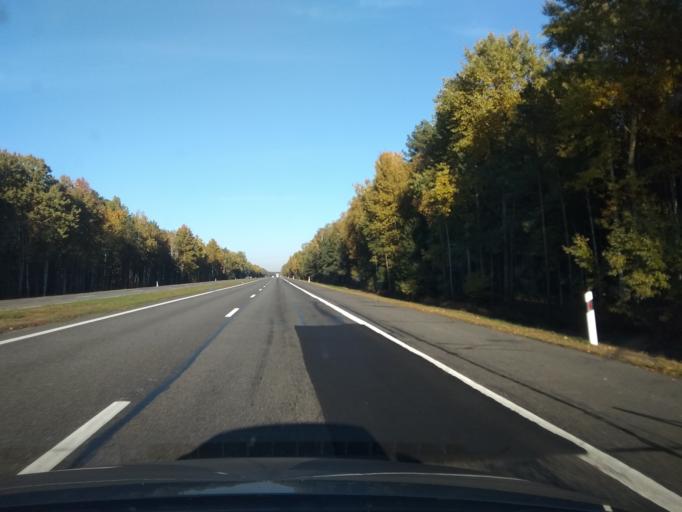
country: BY
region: Brest
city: Nyakhachava
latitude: 52.6308
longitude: 25.2126
